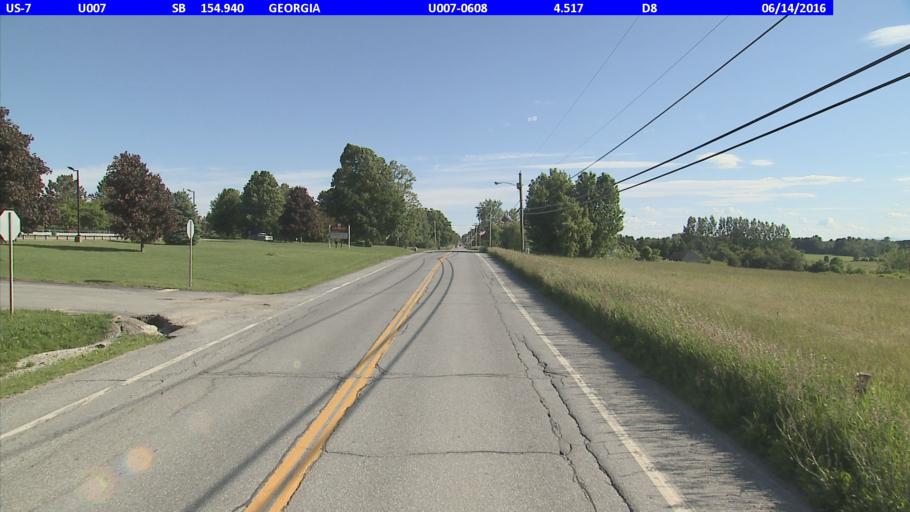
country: US
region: Vermont
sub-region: Franklin County
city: Saint Albans
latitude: 44.7363
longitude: -73.1158
